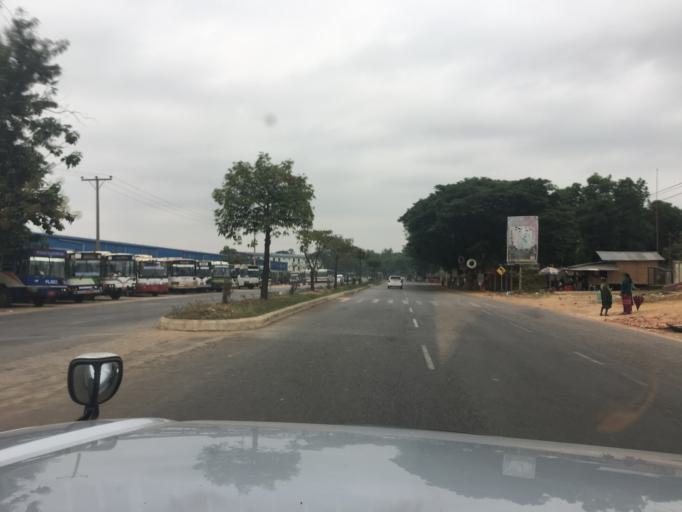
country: MM
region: Bago
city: Thanatpin
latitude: 17.1885
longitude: 96.3927
